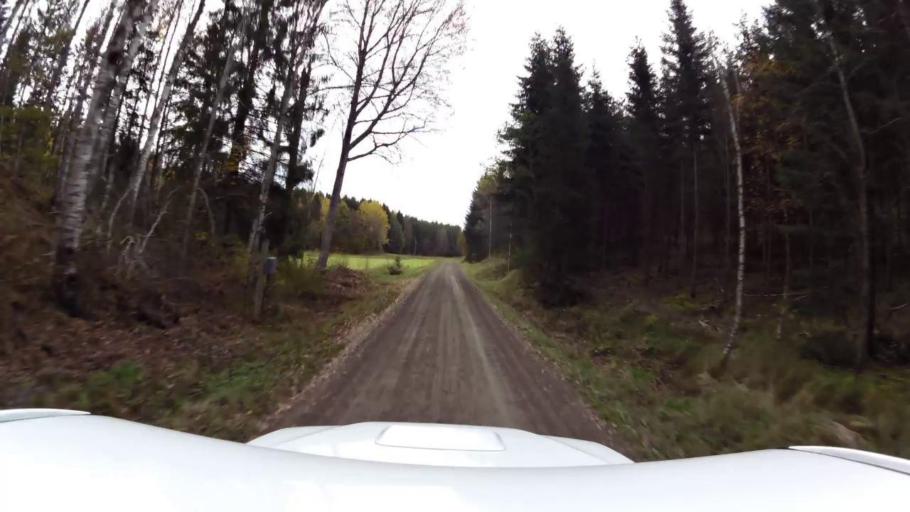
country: SE
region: OEstergoetland
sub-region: Linkopings Kommun
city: Ljungsbro
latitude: 58.5746
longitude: 15.4070
